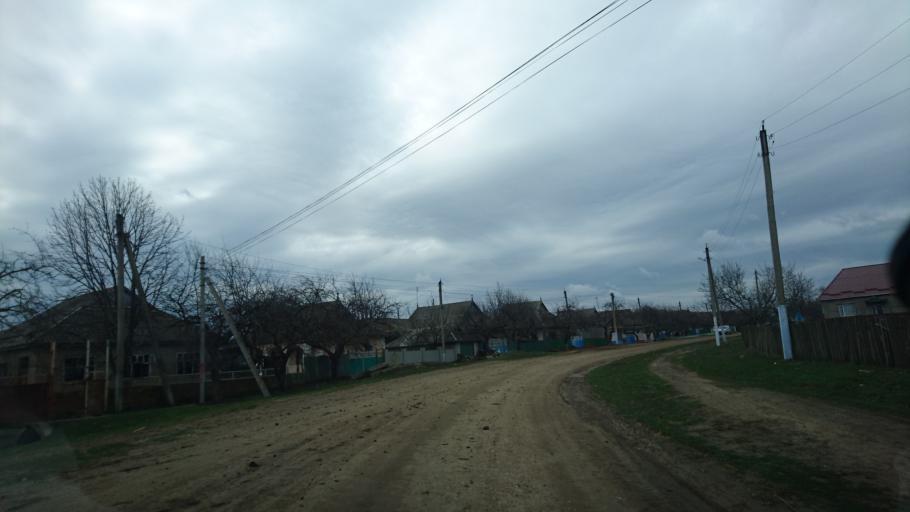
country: MD
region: Cantemir
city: Visniovca
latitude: 46.2858
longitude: 28.3782
